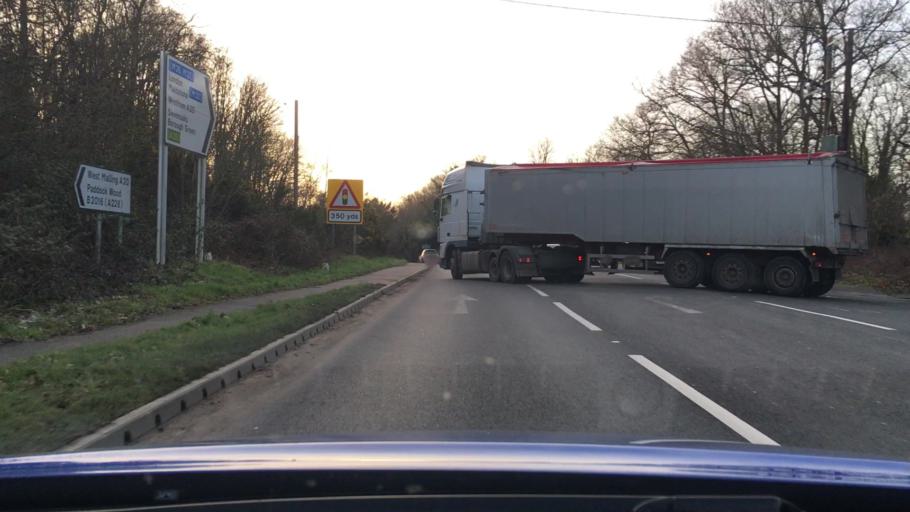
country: GB
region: England
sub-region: Kent
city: Borough Green
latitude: 51.2982
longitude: 0.3457
